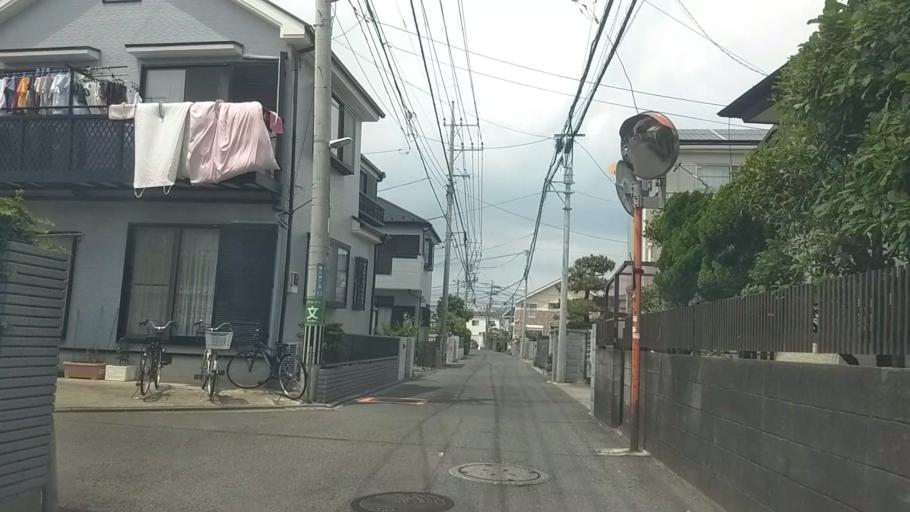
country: JP
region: Kanagawa
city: Chigasaki
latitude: 35.3530
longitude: 139.3967
